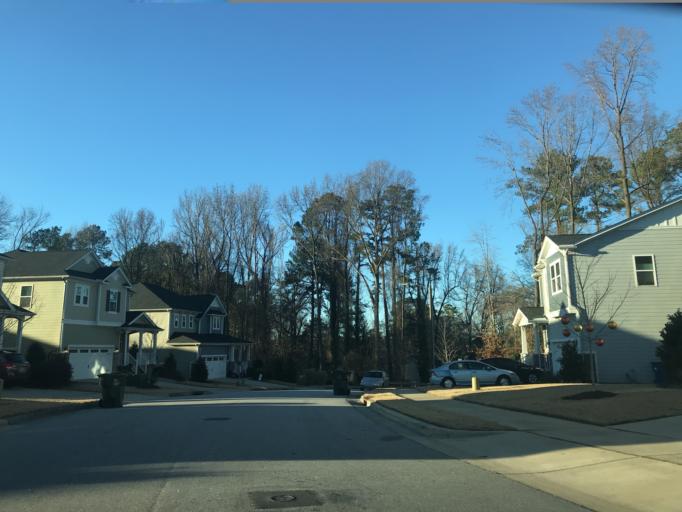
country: US
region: North Carolina
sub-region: Wake County
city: Raleigh
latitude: 35.7956
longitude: -78.6203
